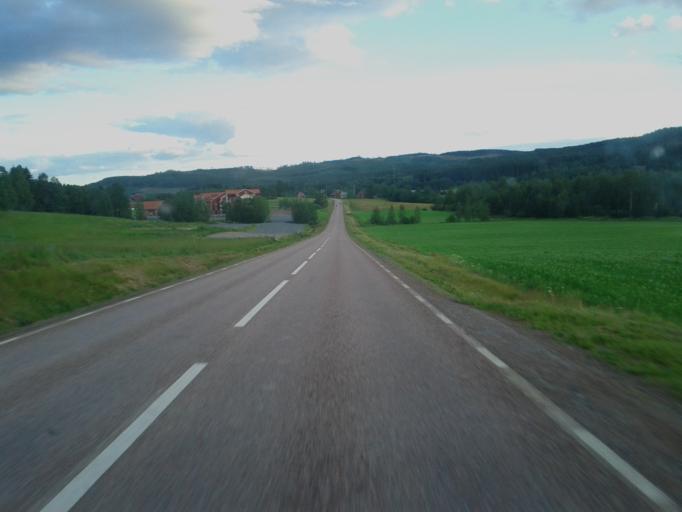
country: SE
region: Dalarna
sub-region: Borlange Kommun
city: Borlaenge
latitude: 60.3968
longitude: 15.3844
